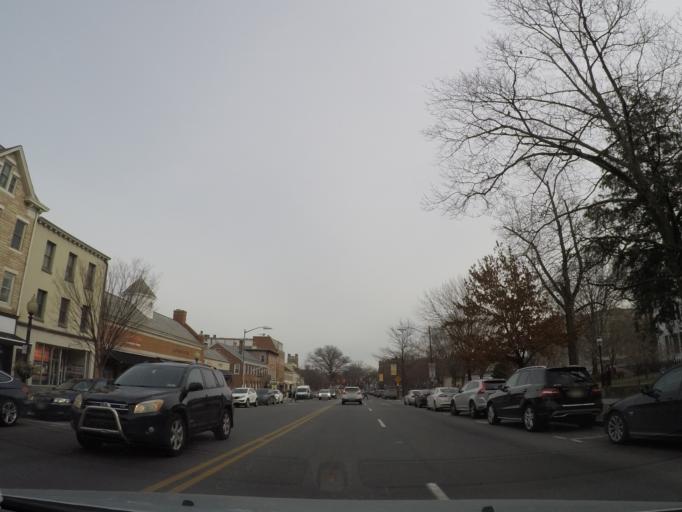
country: US
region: New Jersey
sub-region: Mercer County
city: Princeton
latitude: 40.3493
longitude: -74.6589
